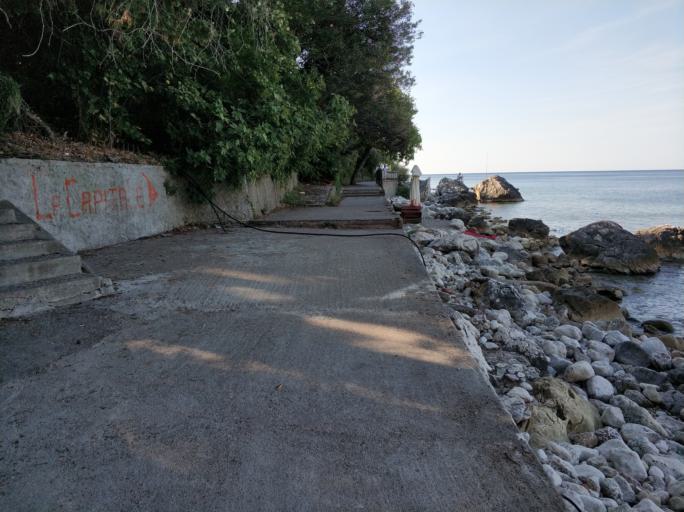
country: ME
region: Budva
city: Budva
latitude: 42.2741
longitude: 18.8883
